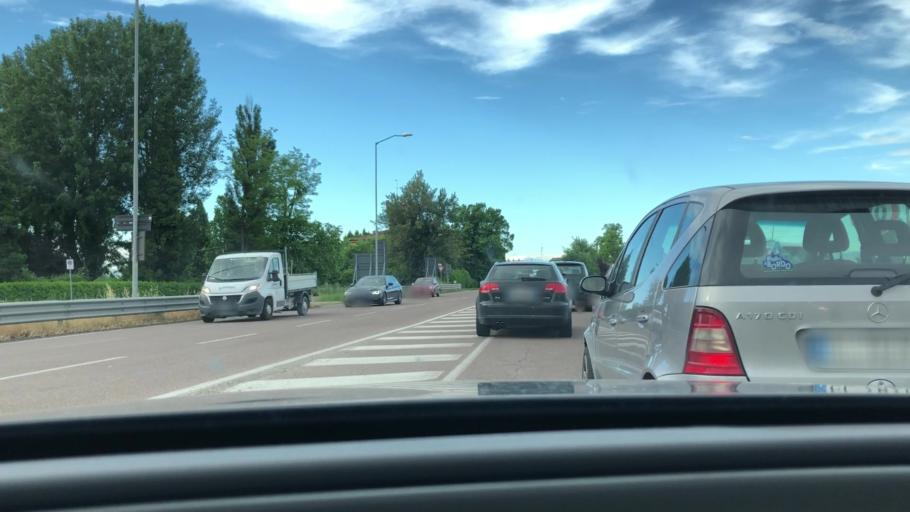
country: IT
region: Emilia-Romagna
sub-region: Provincia di Modena
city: Modena
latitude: 44.6104
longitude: 10.9359
